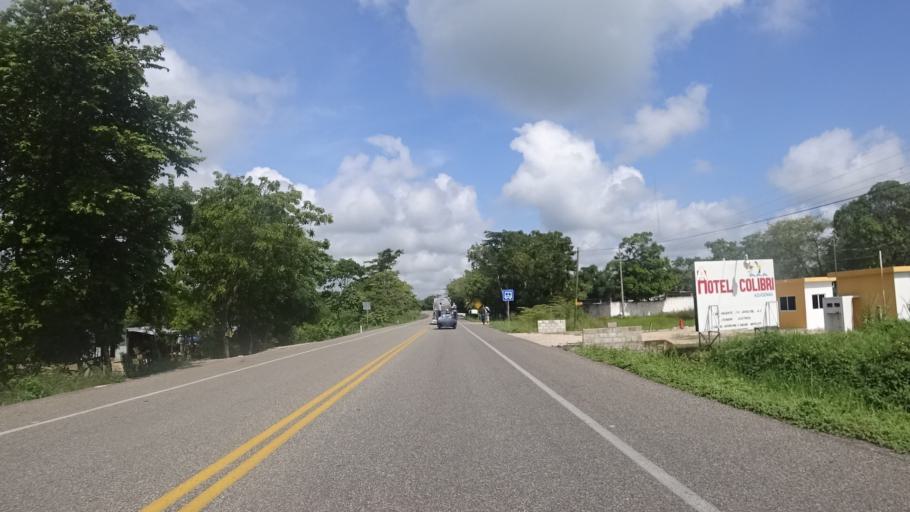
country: MX
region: Chiapas
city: Palenque
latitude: 17.5594
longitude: -92.0059
